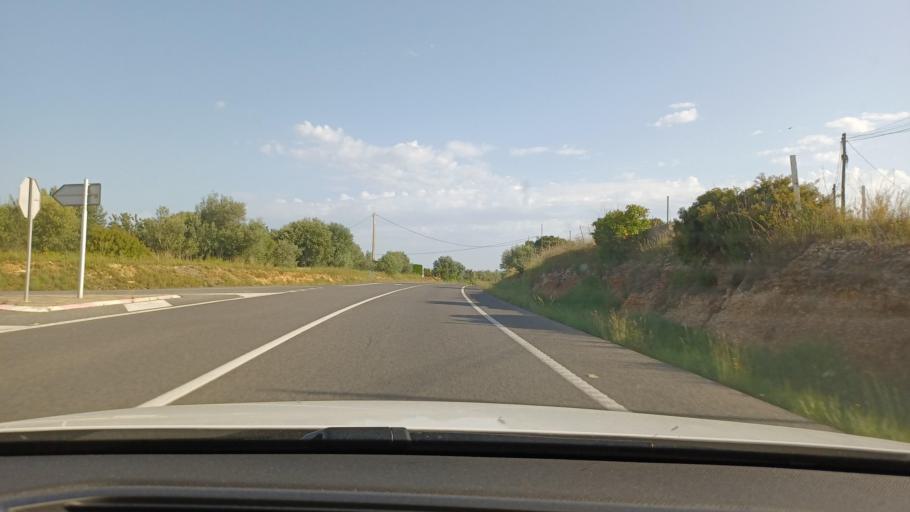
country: ES
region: Catalonia
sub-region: Provincia de Tarragona
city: Amposta
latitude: 40.7165
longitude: 0.5633
